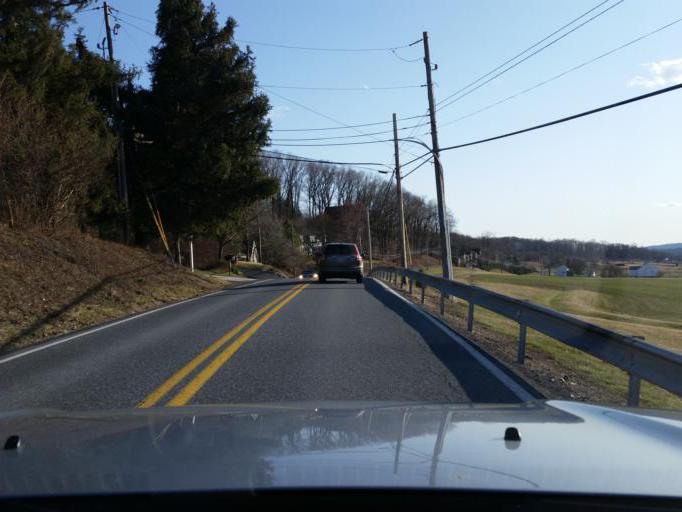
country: US
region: Pennsylvania
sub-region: Dauphin County
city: Hummelstown
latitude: 40.2568
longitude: -76.6887
